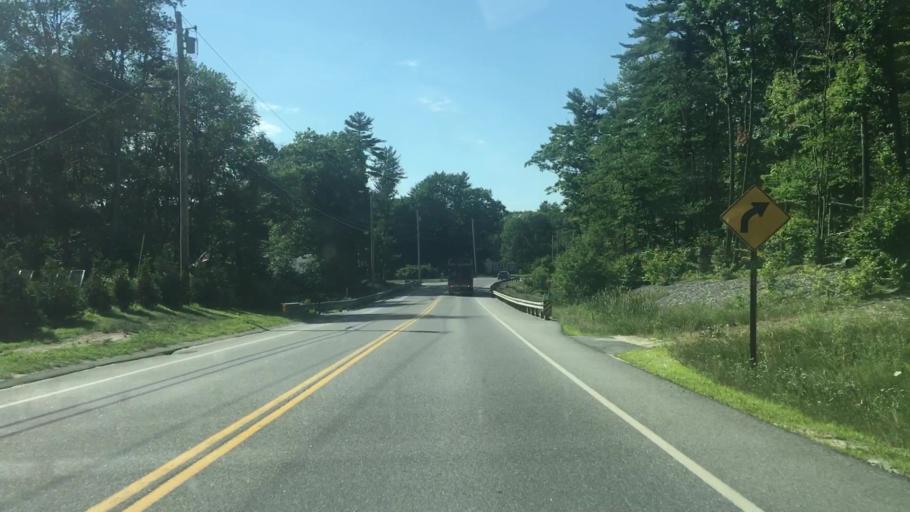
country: US
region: Maine
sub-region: York County
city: Buxton
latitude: 43.5907
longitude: -70.5242
